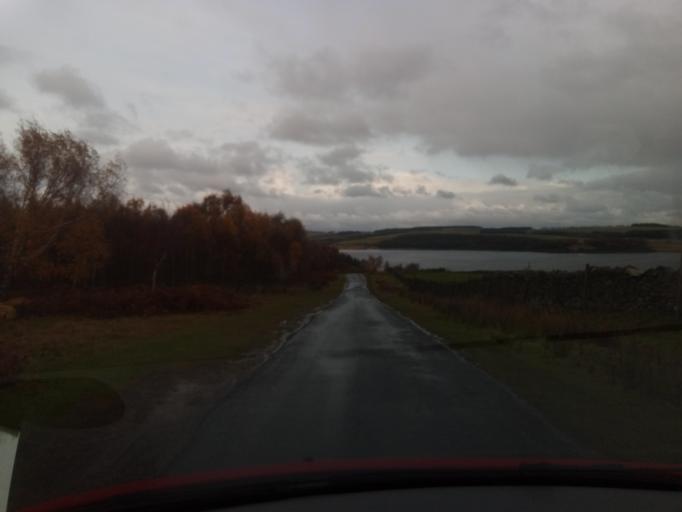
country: GB
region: England
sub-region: County Durham
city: Muggleswick
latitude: 54.8564
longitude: -1.9848
